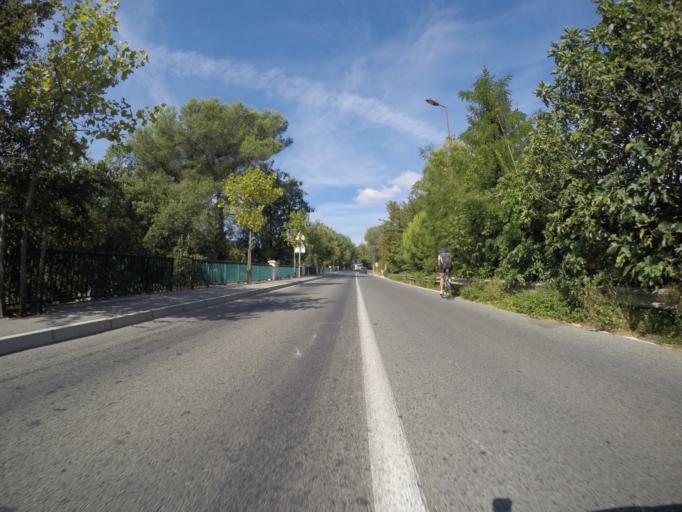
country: FR
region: Provence-Alpes-Cote d'Azur
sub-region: Departement des Alpes-Maritimes
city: Le Rouret
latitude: 43.6734
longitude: 7.0002
